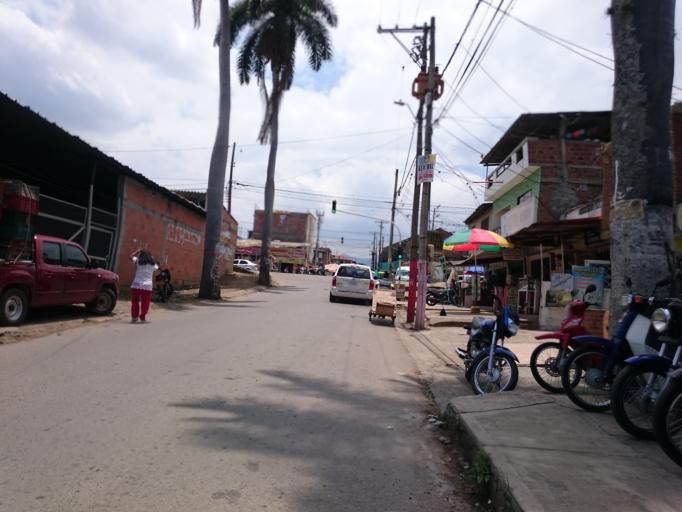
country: CO
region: Cauca
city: Santander de Quilichao
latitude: 3.0071
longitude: -76.4870
